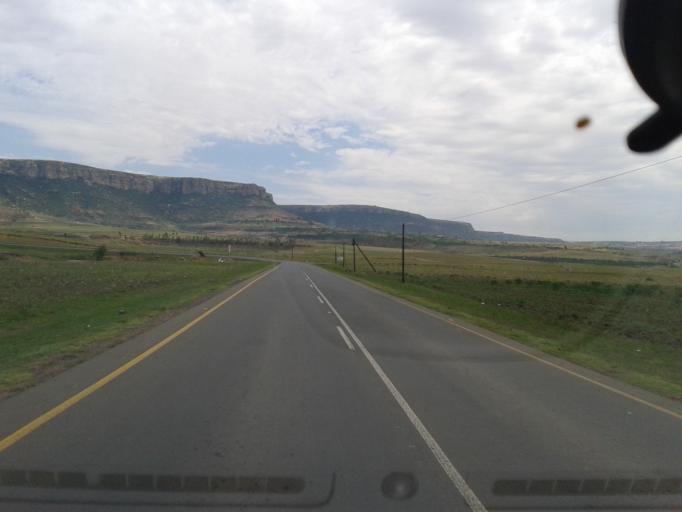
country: LS
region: Maseru
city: Maseru
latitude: -29.3527
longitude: 27.6121
